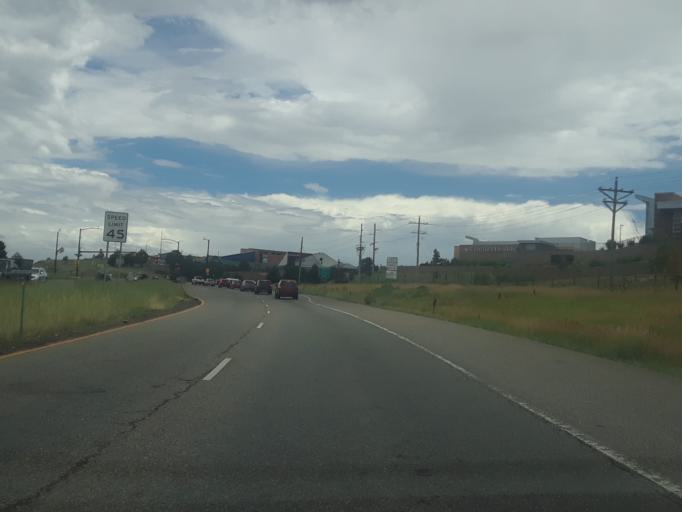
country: US
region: Colorado
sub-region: Jefferson County
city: Golden
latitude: 39.7312
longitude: -105.2114
